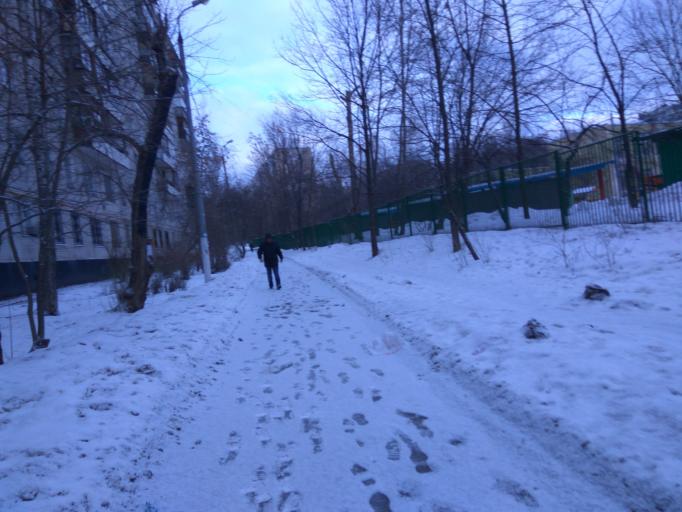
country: RU
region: Moscow
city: Zagor'ye
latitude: 55.5811
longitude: 37.6665
